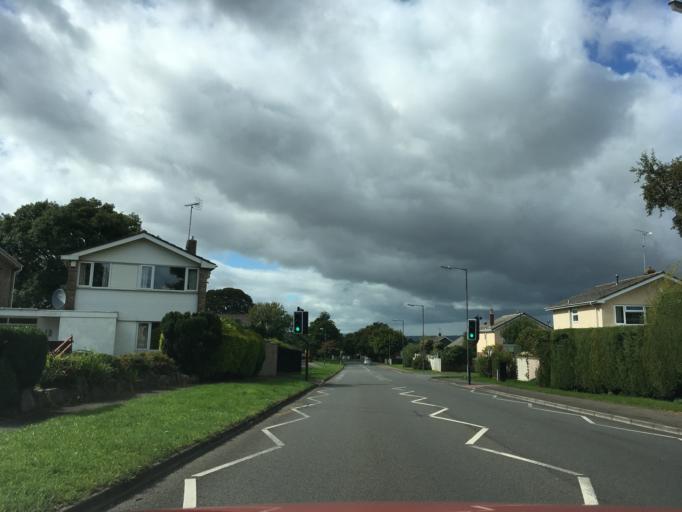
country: GB
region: England
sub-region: South Gloucestershire
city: Thornbury
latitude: 51.6054
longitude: -2.5109
